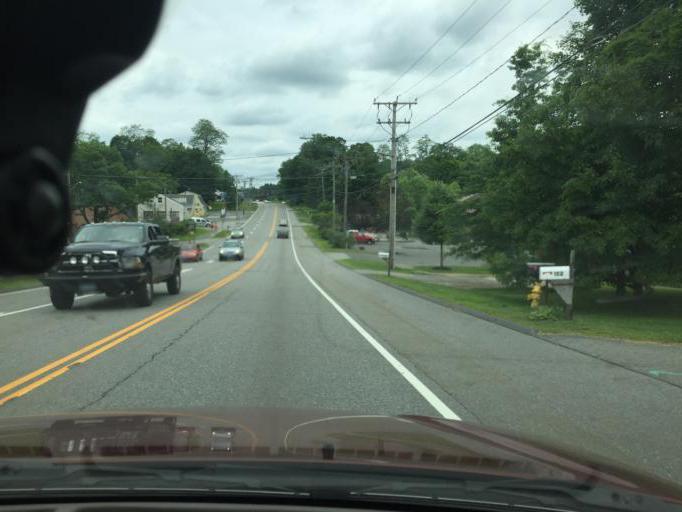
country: US
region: Connecticut
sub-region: Litchfield County
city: Litchfield
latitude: 41.7465
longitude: -73.1959
